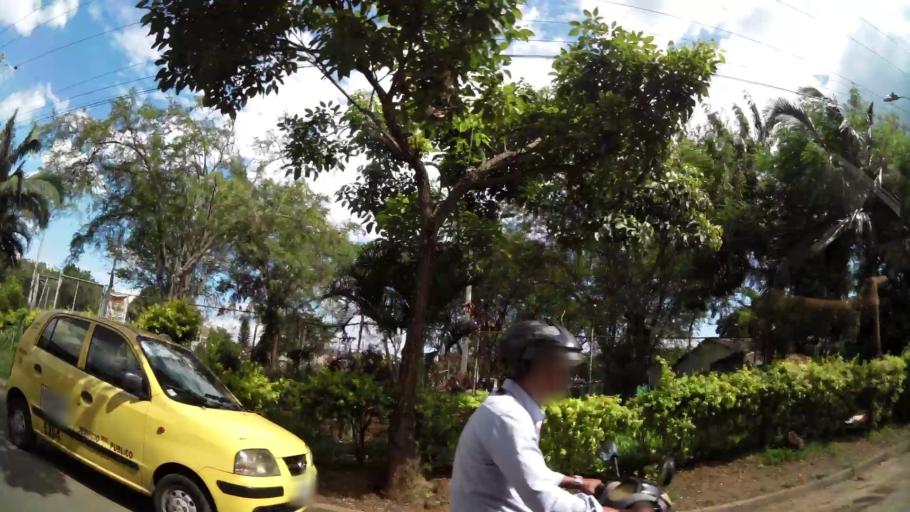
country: CO
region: Valle del Cauca
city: Cali
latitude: 3.3971
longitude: -76.5134
